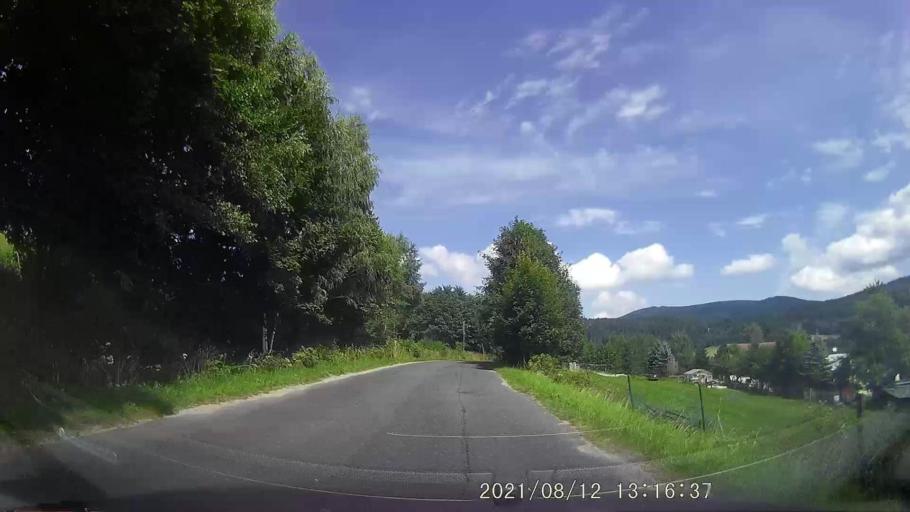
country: PL
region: Lower Silesian Voivodeship
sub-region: Powiat klodzki
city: Stronie Slaskie
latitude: 50.2649
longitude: 16.8792
